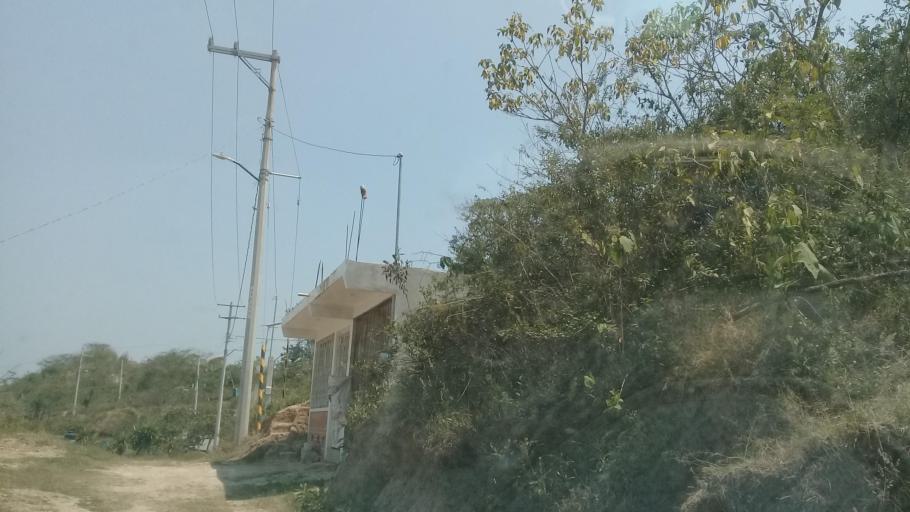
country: MX
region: Veracruz
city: El Castillo
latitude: 19.5504
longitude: -96.8582
